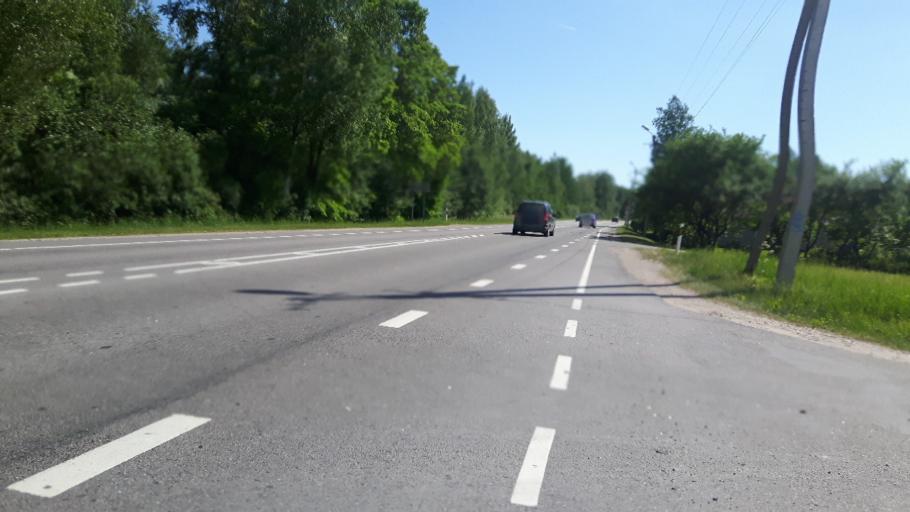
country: EE
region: Paernumaa
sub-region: Paikuse vald
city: Paikuse
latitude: 58.3890
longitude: 24.6408
